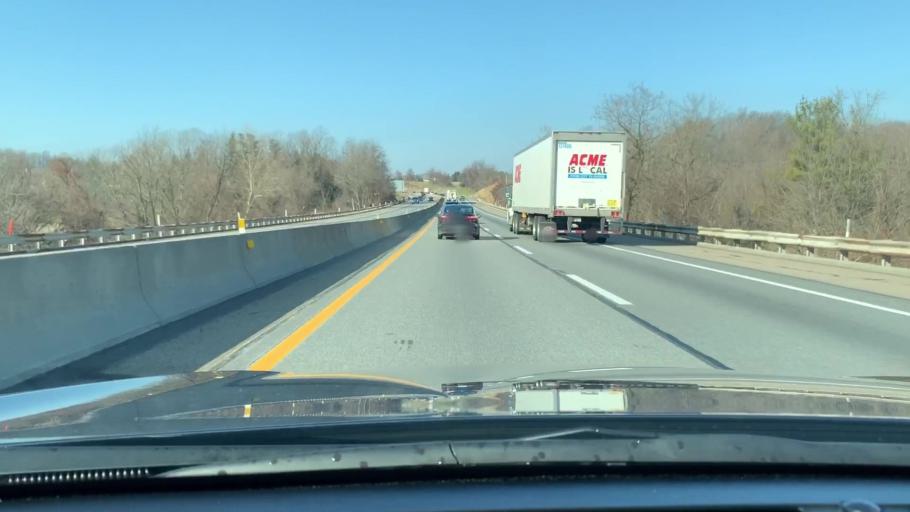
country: US
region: Pennsylvania
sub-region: Chester County
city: Downingtown
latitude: 40.0803
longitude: -75.7051
